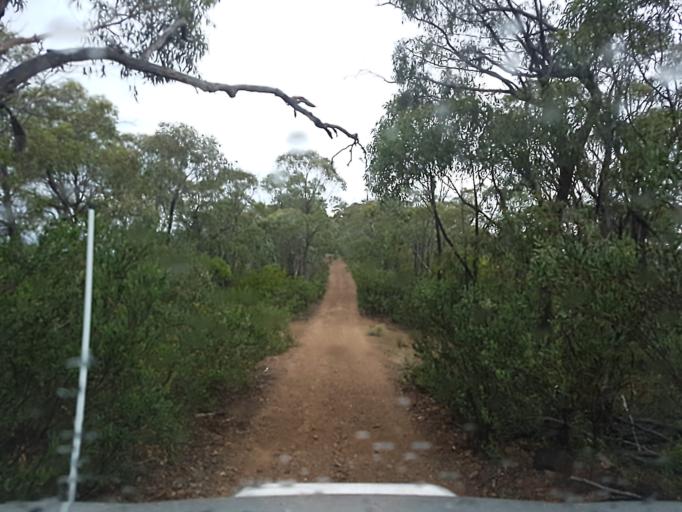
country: AU
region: New South Wales
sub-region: Snowy River
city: Jindabyne
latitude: -36.9231
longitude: 148.3468
